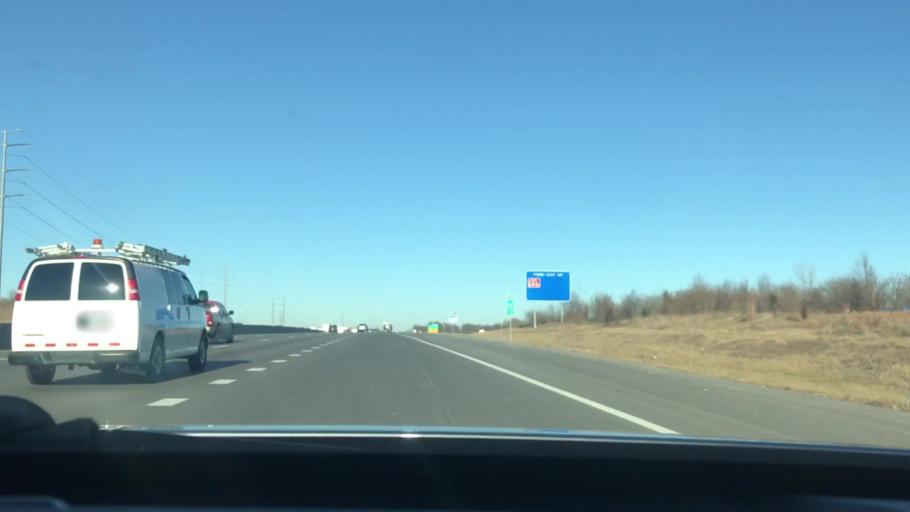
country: US
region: Missouri
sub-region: Jackson County
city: Grandview
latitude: 38.9609
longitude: -94.5281
